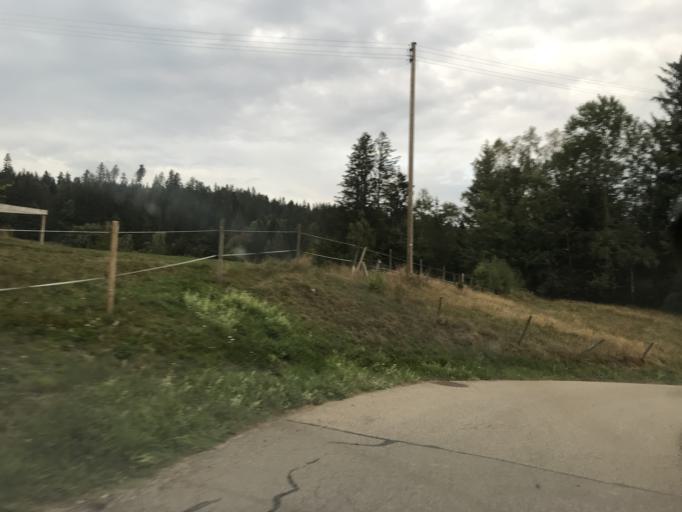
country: DE
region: Baden-Wuerttemberg
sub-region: Freiburg Region
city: Todtmoos
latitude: 47.7214
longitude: 7.9836
